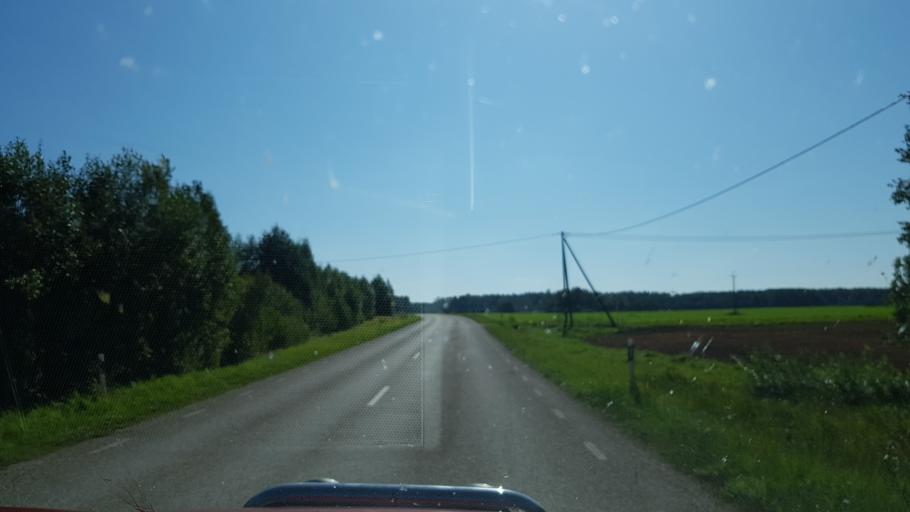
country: EE
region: Polvamaa
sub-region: Polva linn
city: Polva
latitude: 58.2240
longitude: 27.2298
